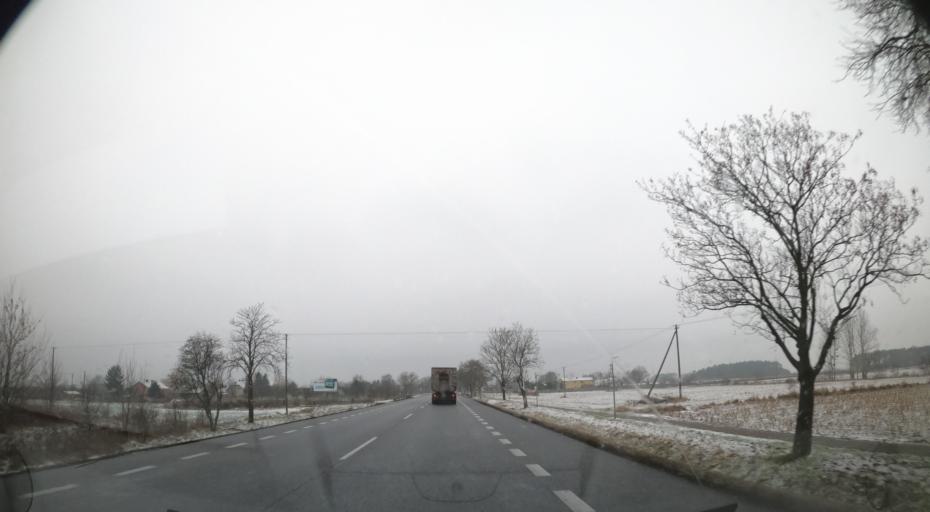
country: PL
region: Masovian Voivodeship
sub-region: Powiat sochaczewski
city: Teresin
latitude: 52.2199
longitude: 20.3432
